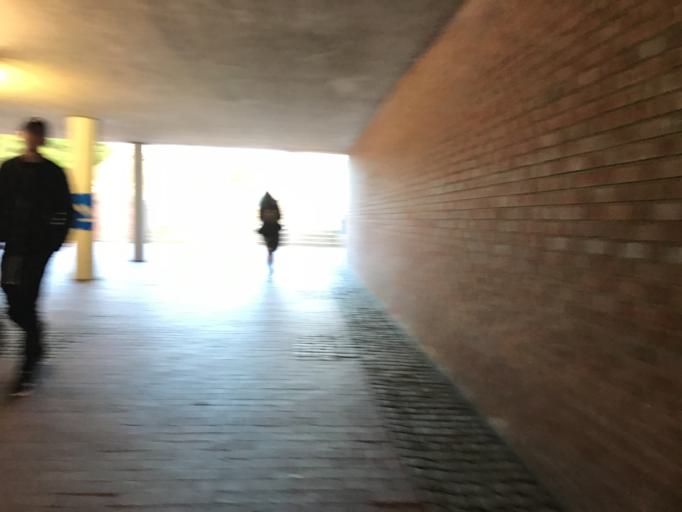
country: DE
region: Schleswig-Holstein
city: Rendsburg
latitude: 54.3028
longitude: 9.6692
